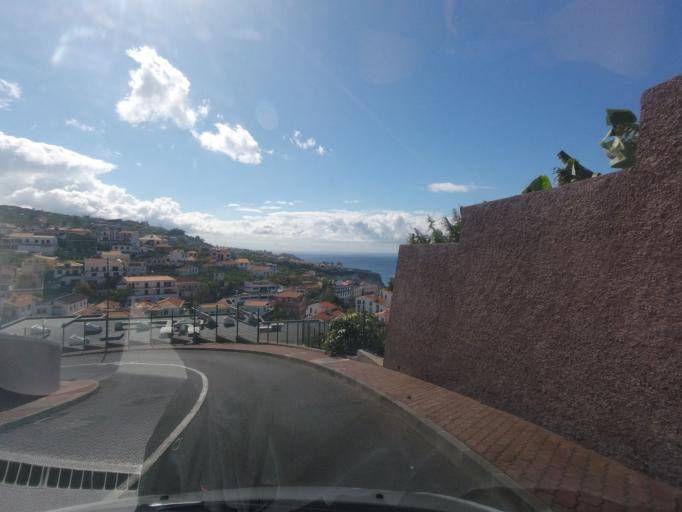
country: PT
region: Madeira
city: Camara de Lobos
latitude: 32.6503
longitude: -16.9721
